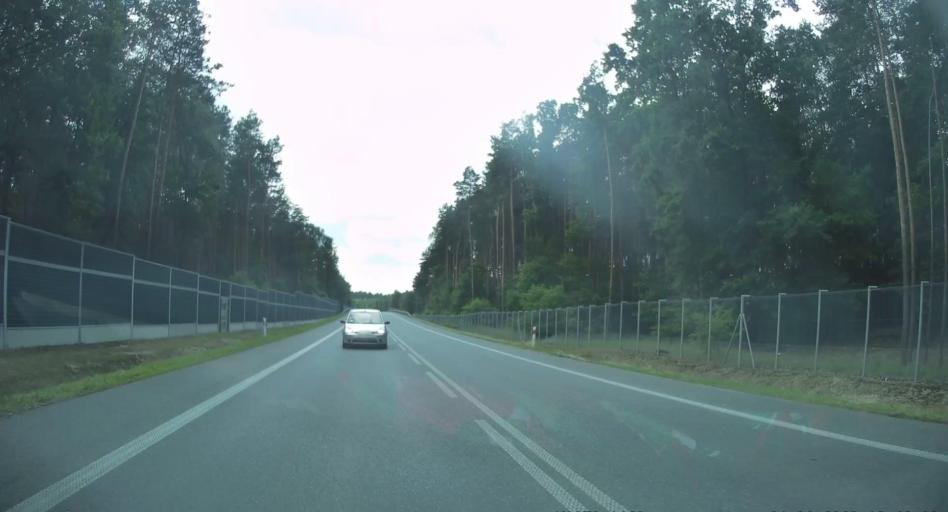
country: PL
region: Subcarpathian Voivodeship
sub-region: Powiat mielecki
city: Mielec
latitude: 50.3002
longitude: 21.4952
